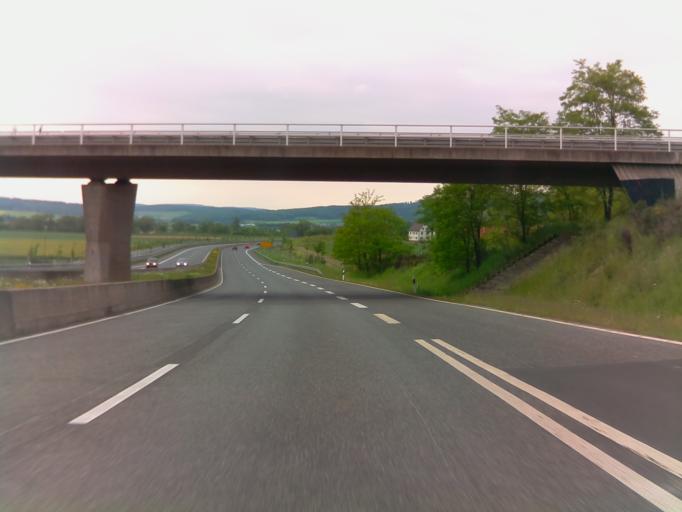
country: DE
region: Hesse
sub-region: Regierungsbezirk Giessen
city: Fronhausen
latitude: 50.7250
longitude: 8.7364
